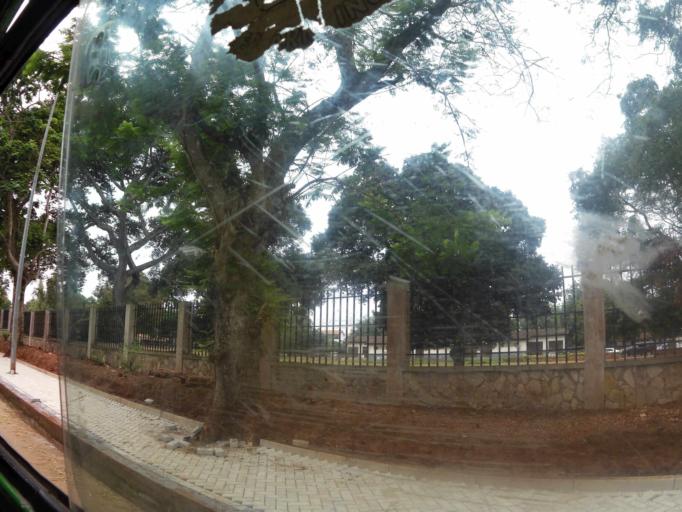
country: GH
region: Greater Accra
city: Medina Estates
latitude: 5.6437
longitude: -0.1880
